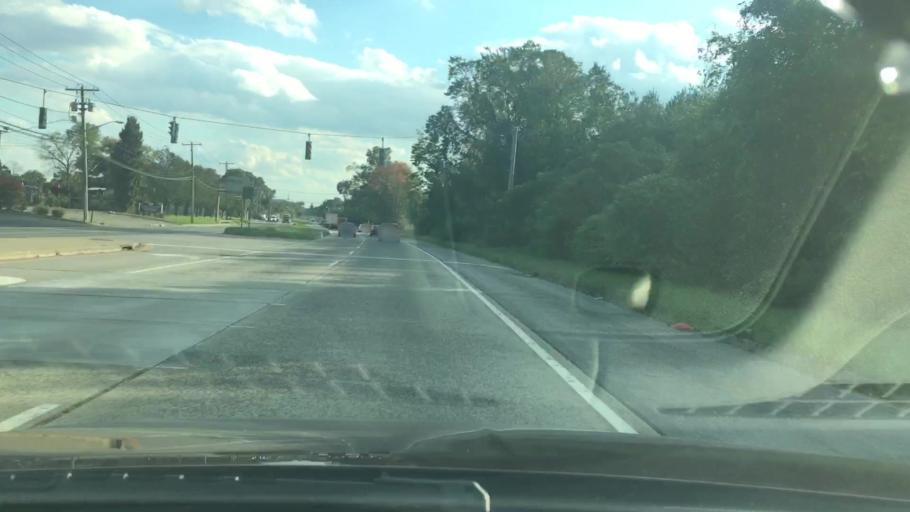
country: US
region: New York
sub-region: Suffolk County
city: Dix Hills
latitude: 40.7910
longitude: -73.3414
